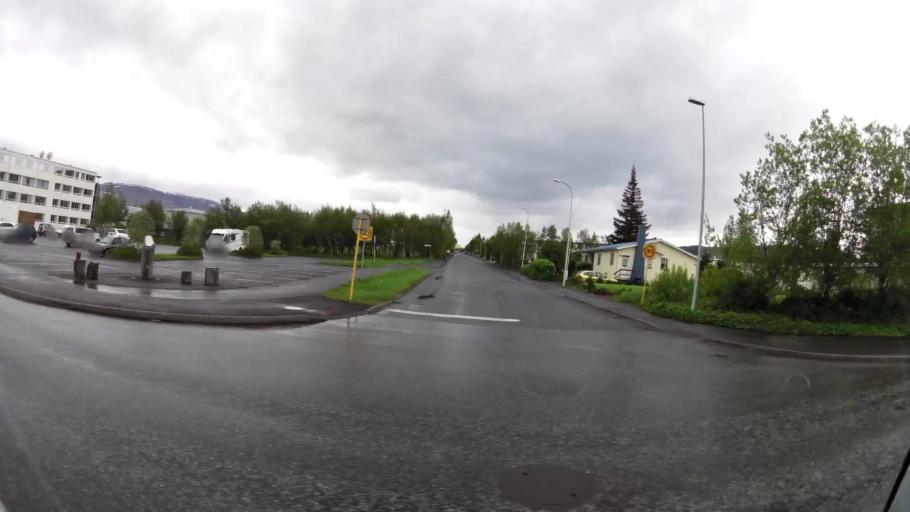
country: IS
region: Northeast
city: Akureyri
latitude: 65.6792
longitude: -18.1026
